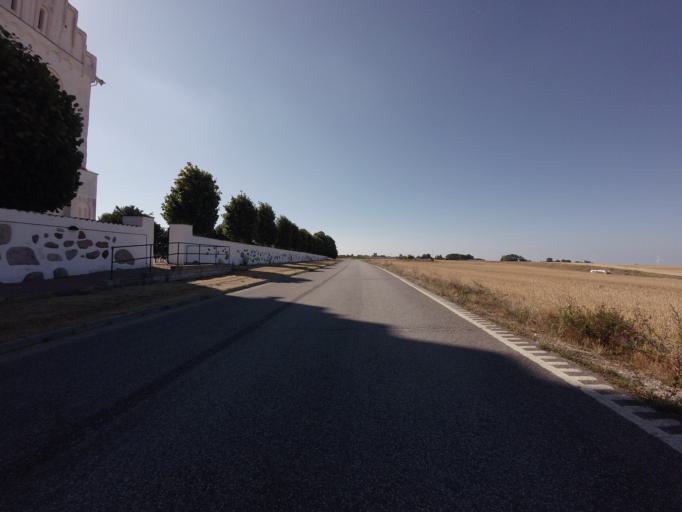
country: SE
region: Skane
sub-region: Trelleborgs Kommun
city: Skare
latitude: 55.4053
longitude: 13.0647
